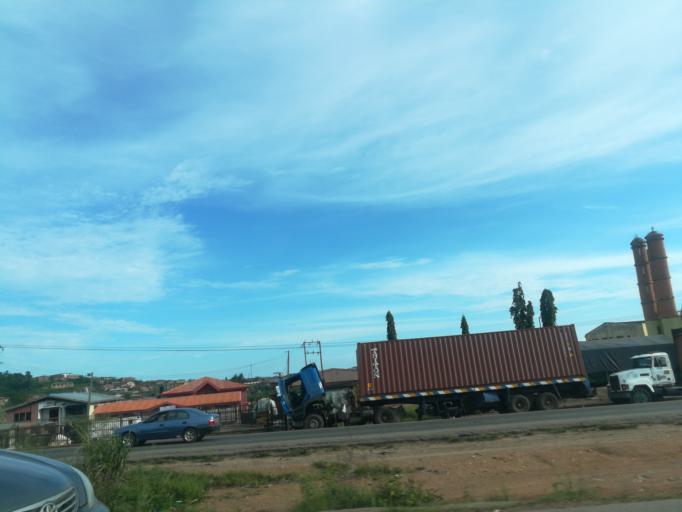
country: NG
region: Oyo
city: Ibadan
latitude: 7.3432
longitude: 3.9107
